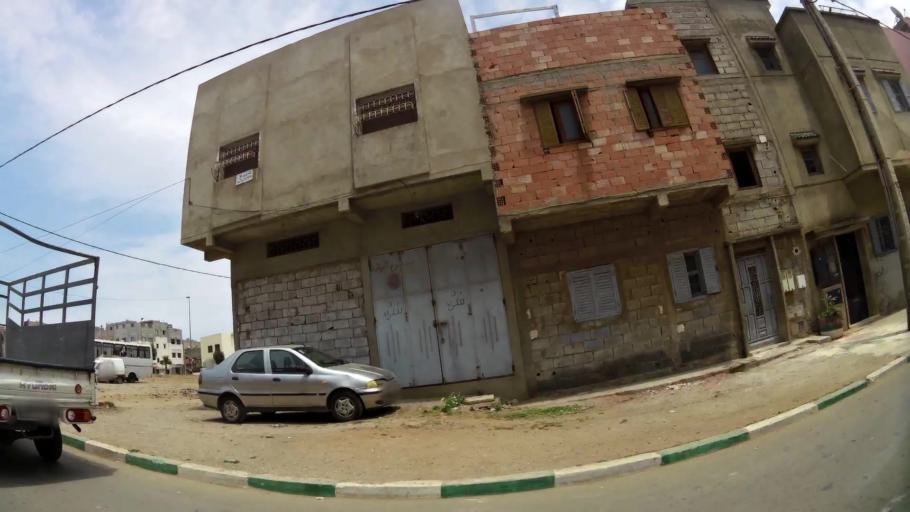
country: MA
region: Rabat-Sale-Zemmour-Zaer
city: Sale
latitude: 34.0698
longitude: -6.7742
